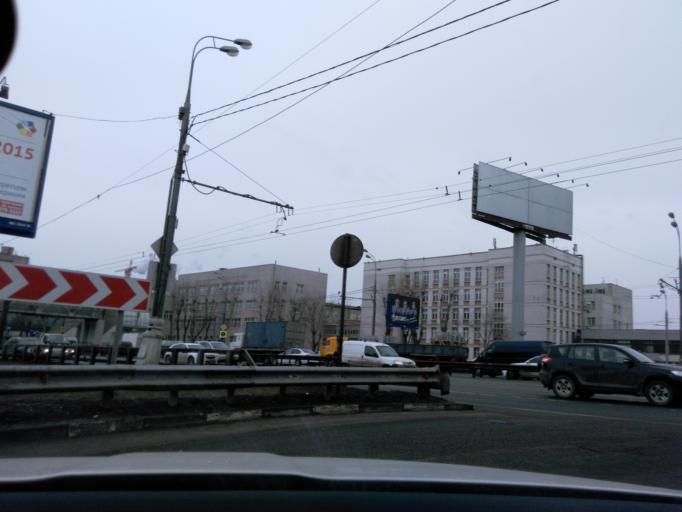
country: RU
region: Moscow
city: Zamoskvorech'ye
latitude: 55.7049
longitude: 37.6354
